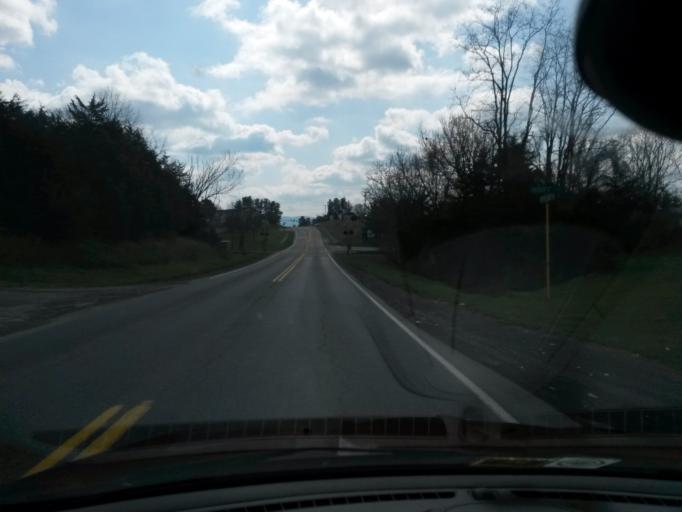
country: US
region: Virginia
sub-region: Augusta County
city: Weyers Cave
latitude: 38.2872
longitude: -78.9174
